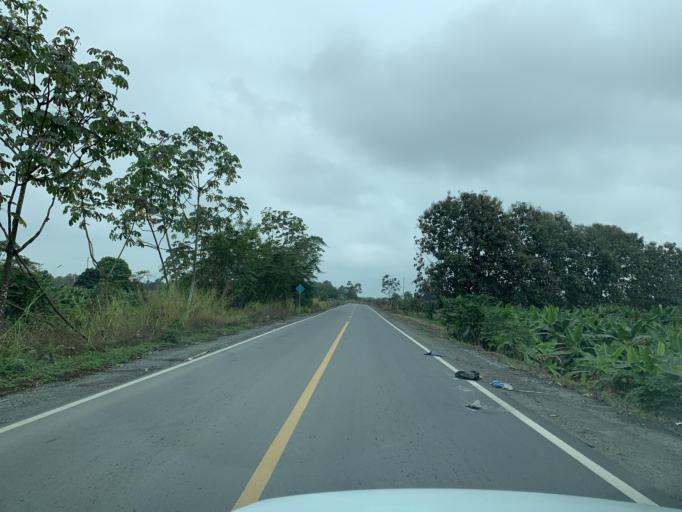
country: EC
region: Guayas
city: Coronel Marcelino Mariduena
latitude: -2.2984
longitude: -79.5036
